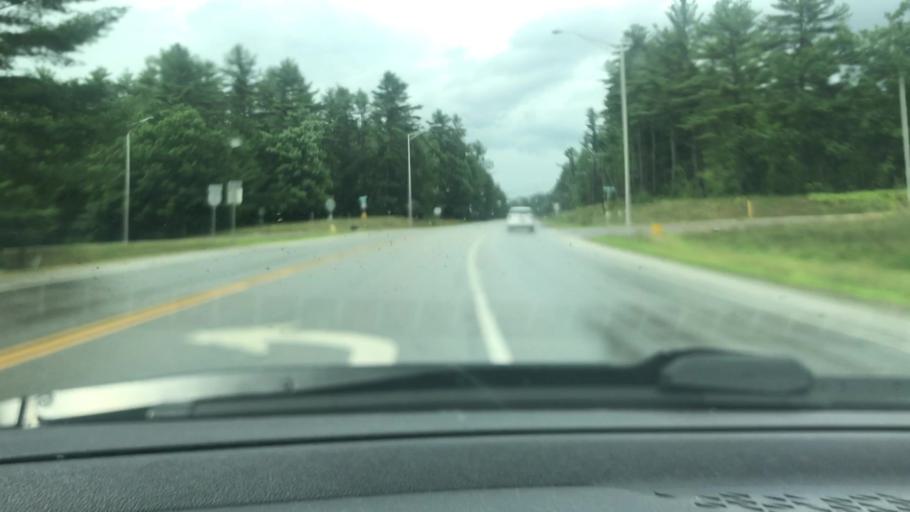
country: US
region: New Hampshire
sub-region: Merrimack County
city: Chichester
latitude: 43.2747
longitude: -71.4616
